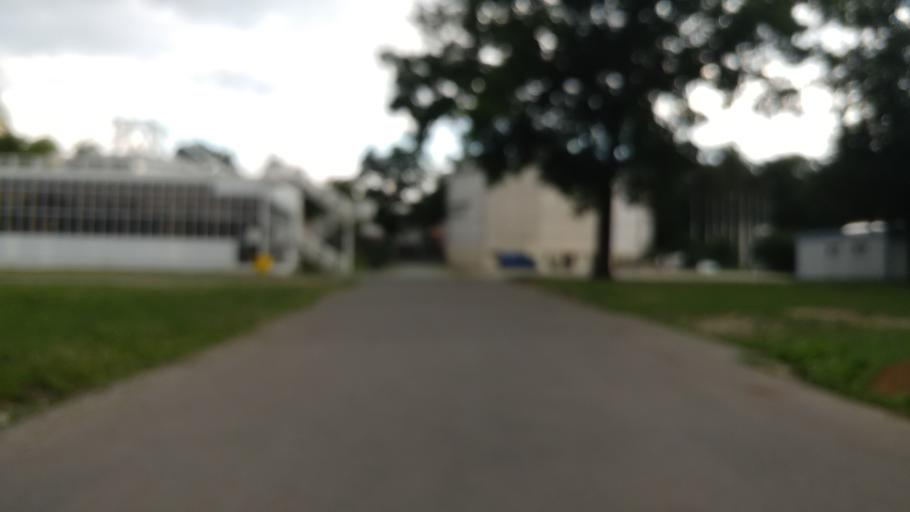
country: CZ
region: Praha
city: Prague
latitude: 50.1076
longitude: 14.4272
